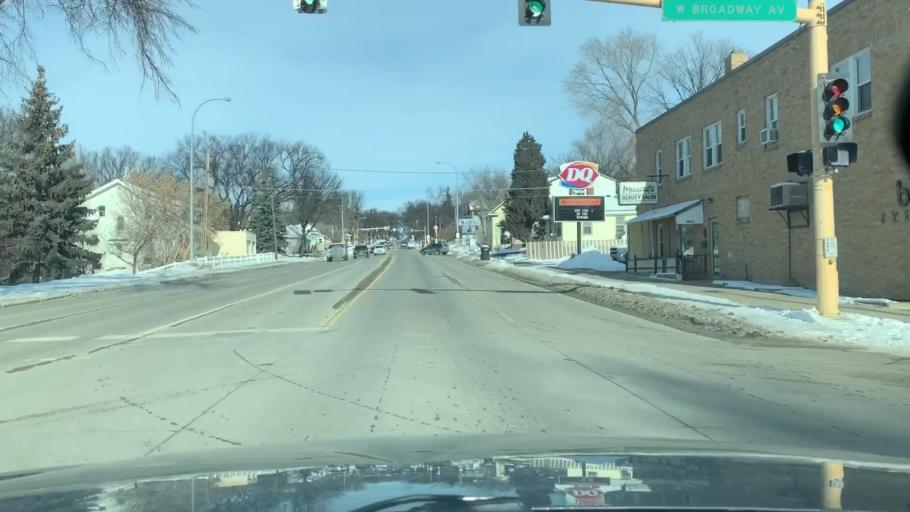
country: US
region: North Dakota
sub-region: Burleigh County
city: Bismarck
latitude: 46.8066
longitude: -100.7944
